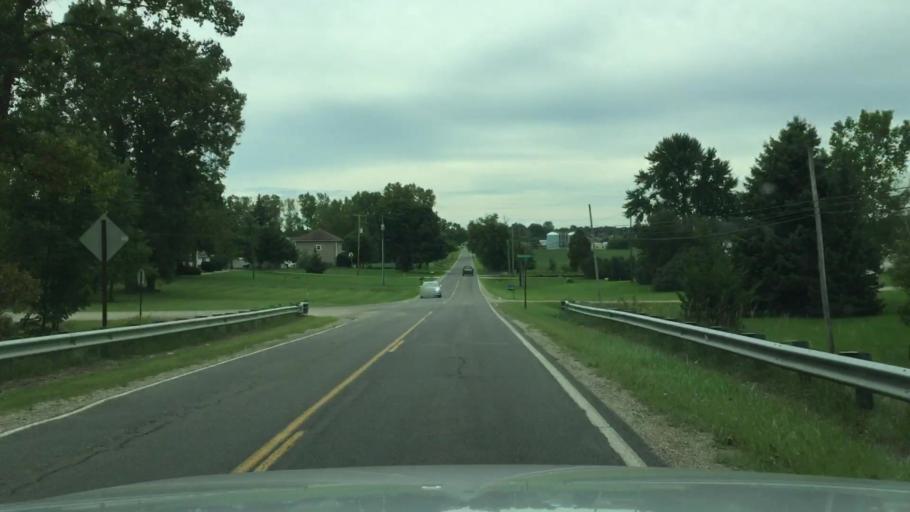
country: US
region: Michigan
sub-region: Shiawassee County
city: Durand
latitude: 42.9337
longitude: -83.9885
